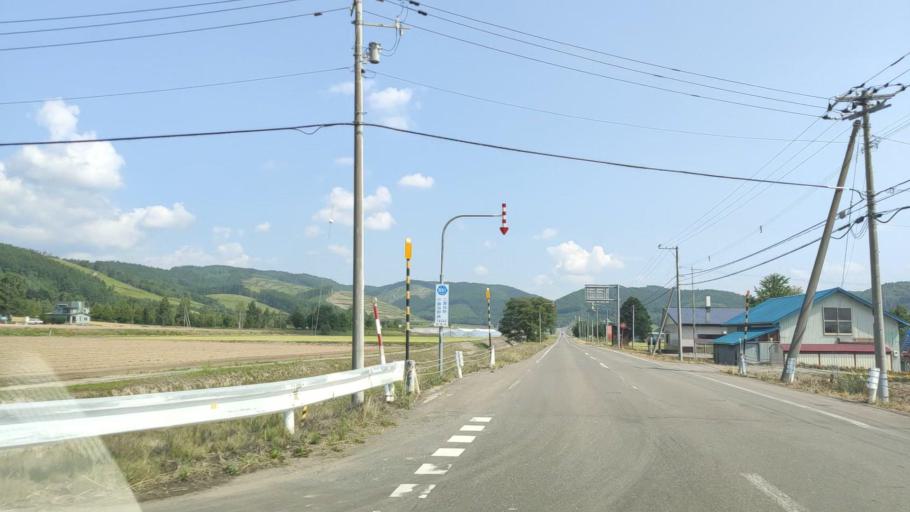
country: JP
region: Hokkaido
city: Shimo-furano
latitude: 43.4061
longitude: 142.3959
